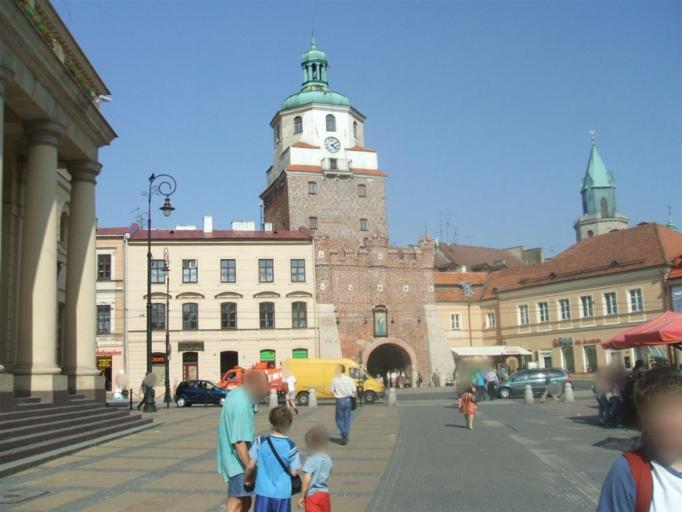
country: PL
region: Lublin Voivodeship
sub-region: Powiat lubelski
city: Lublin
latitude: 51.2475
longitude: 22.5656
